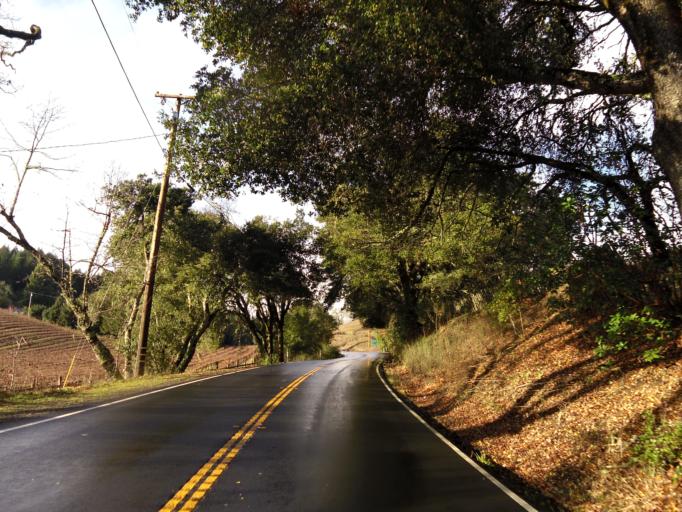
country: US
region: California
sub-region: Sonoma County
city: Cloverdale
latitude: 38.8790
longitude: -123.1128
